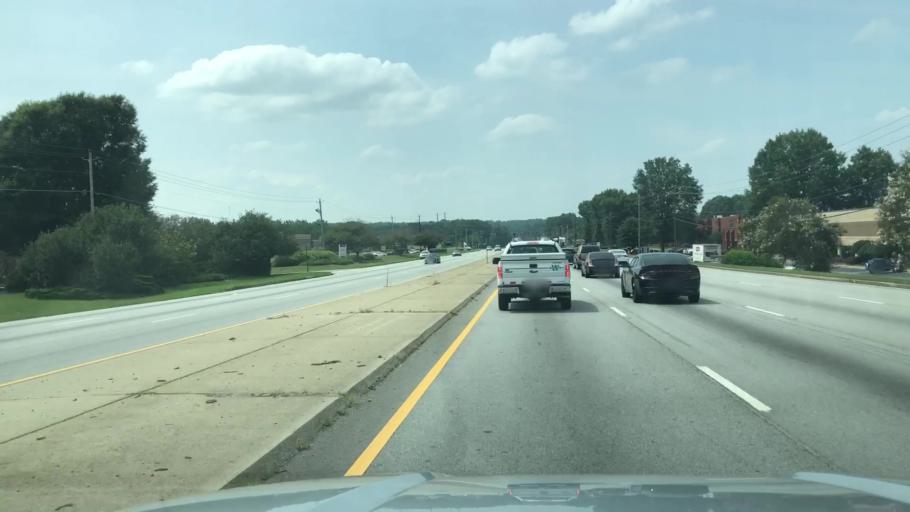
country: US
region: Georgia
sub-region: Cobb County
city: Austell
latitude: 33.7921
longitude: -84.6300
